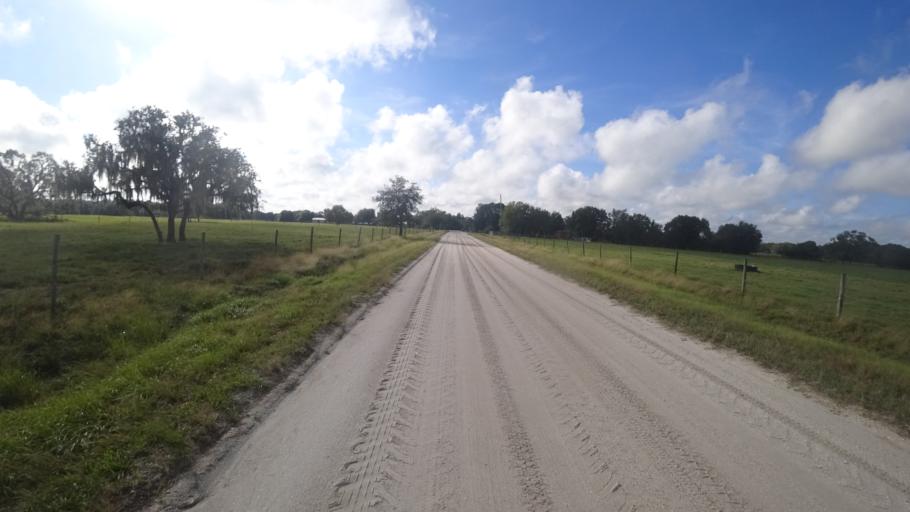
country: US
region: Florida
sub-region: Hillsborough County
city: Wimauma
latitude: 27.4679
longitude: -82.2272
